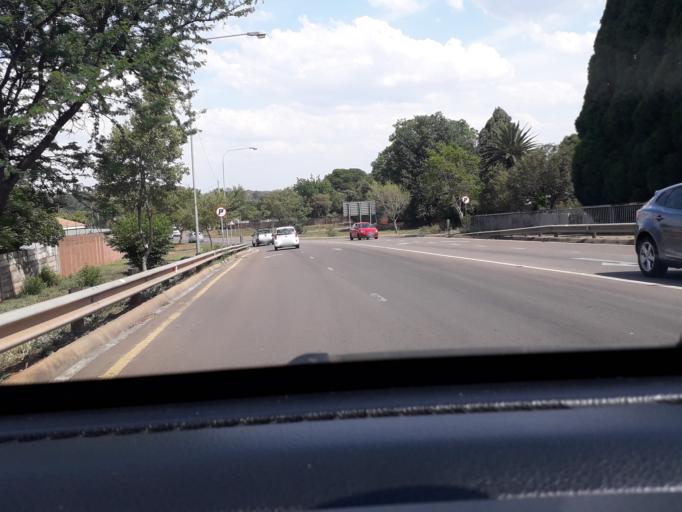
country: ZA
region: Gauteng
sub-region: City of Tshwane Metropolitan Municipality
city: Centurion
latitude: -25.8407
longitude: 28.2118
